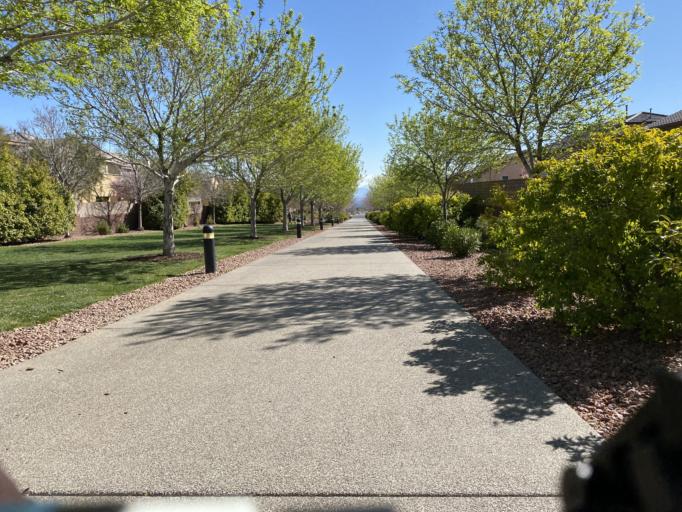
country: US
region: Nevada
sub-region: Clark County
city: Summerlin South
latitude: 36.2920
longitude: -115.3216
